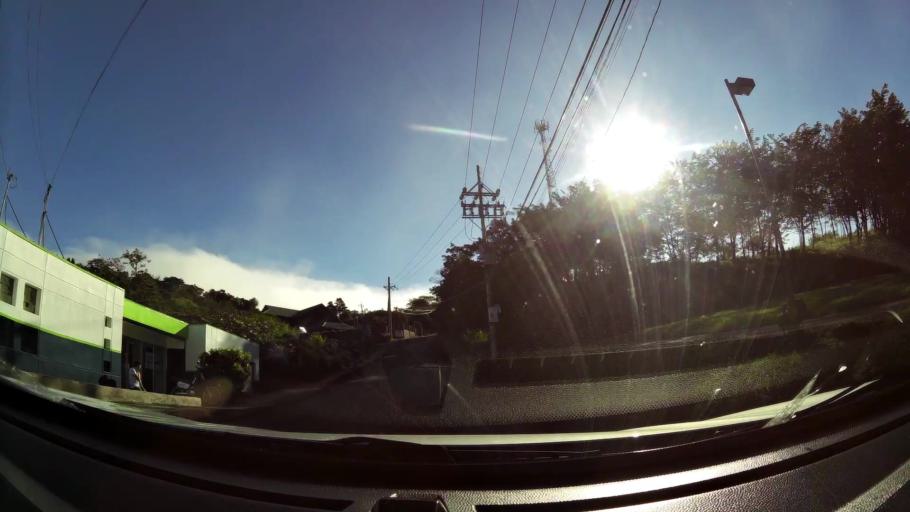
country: CR
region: Guanacaste
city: Juntas
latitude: 10.3156
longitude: -84.8217
